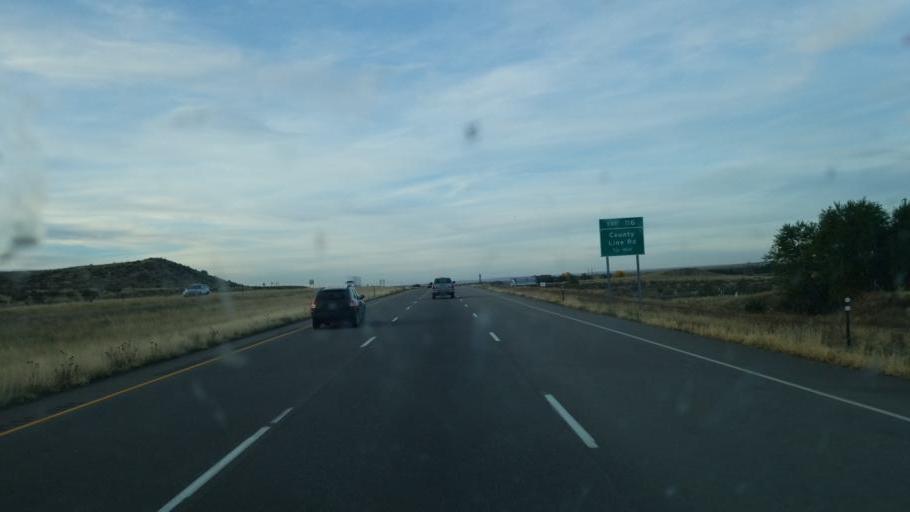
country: US
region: Colorado
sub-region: Pueblo County
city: Pueblo West
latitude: 38.5025
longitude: -104.6268
